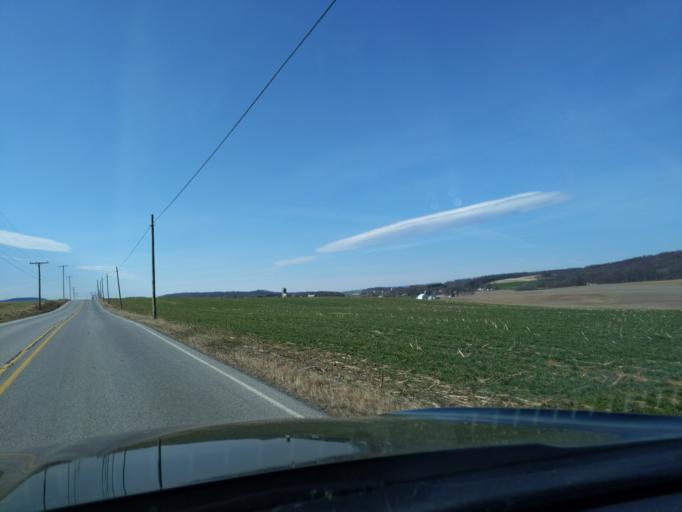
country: US
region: Pennsylvania
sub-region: Blair County
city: Martinsburg
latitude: 40.3282
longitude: -78.2679
